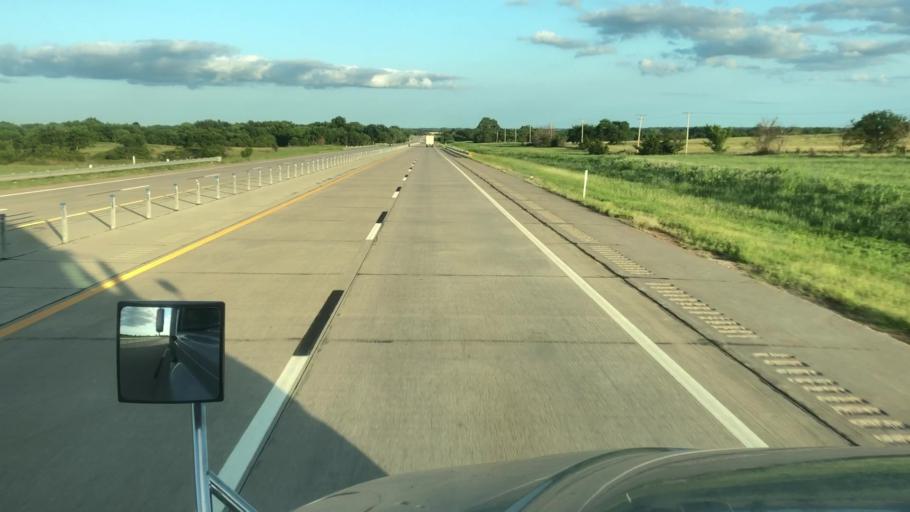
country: US
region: Oklahoma
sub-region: Pawnee County
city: Pawnee
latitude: 36.3306
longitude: -97.0114
